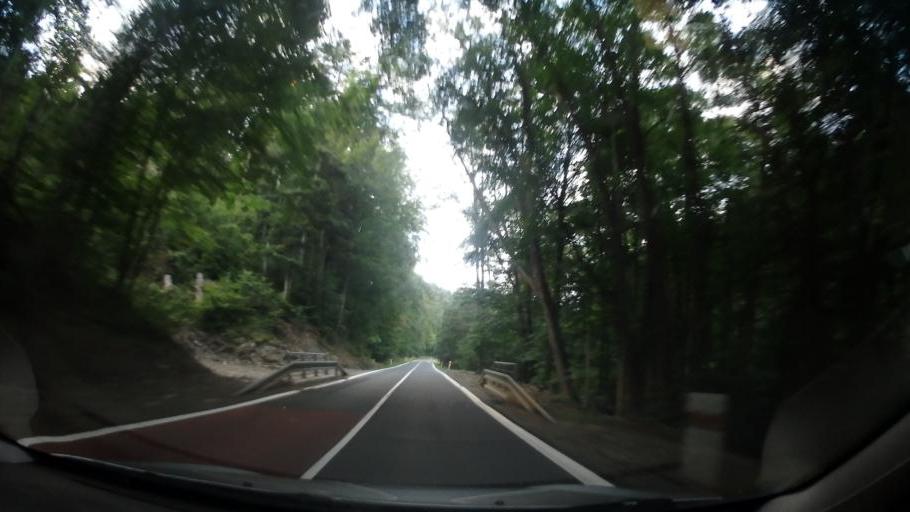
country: CZ
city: Horni Mesto
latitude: 49.8740
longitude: 17.2364
